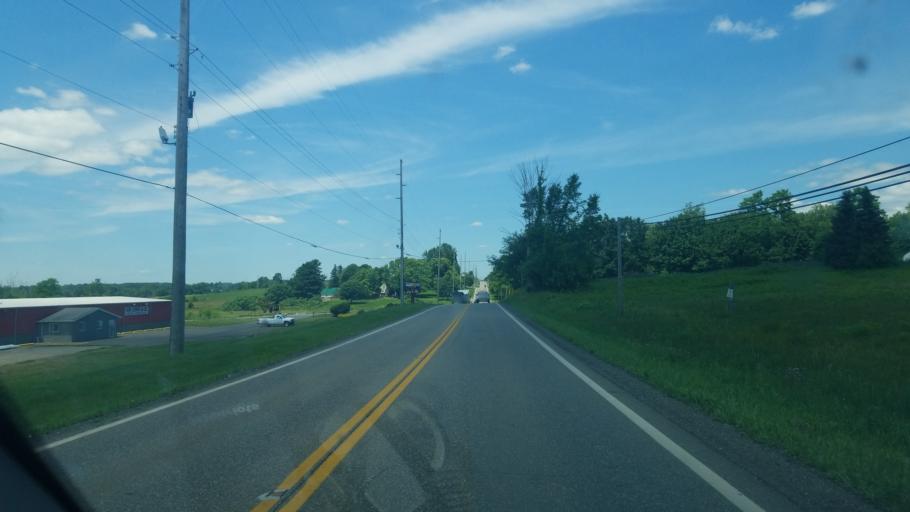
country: US
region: Ohio
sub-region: Columbiana County
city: Lisbon
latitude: 40.7949
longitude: -80.7804
